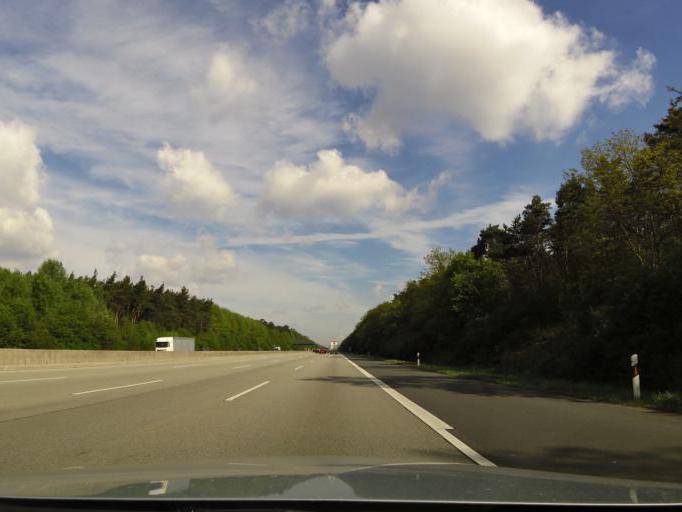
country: DE
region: Hesse
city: Morfelden-Walldorf
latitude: 49.9889
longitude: 8.5999
